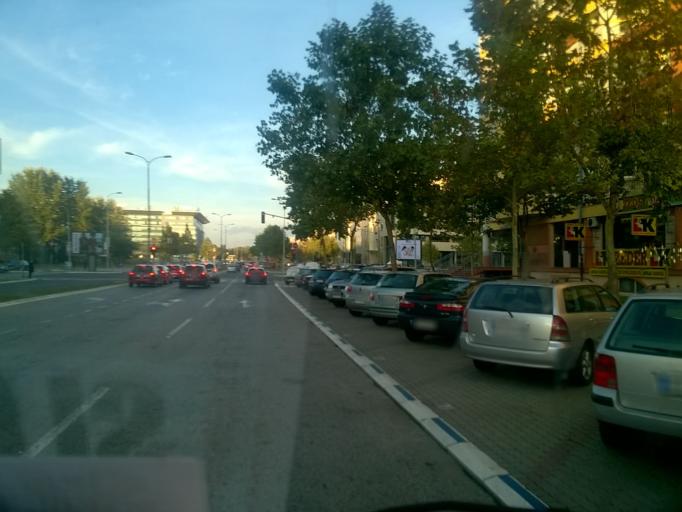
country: RS
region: Central Serbia
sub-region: Belgrade
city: Novi Beograd
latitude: 44.8137
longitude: 20.4248
